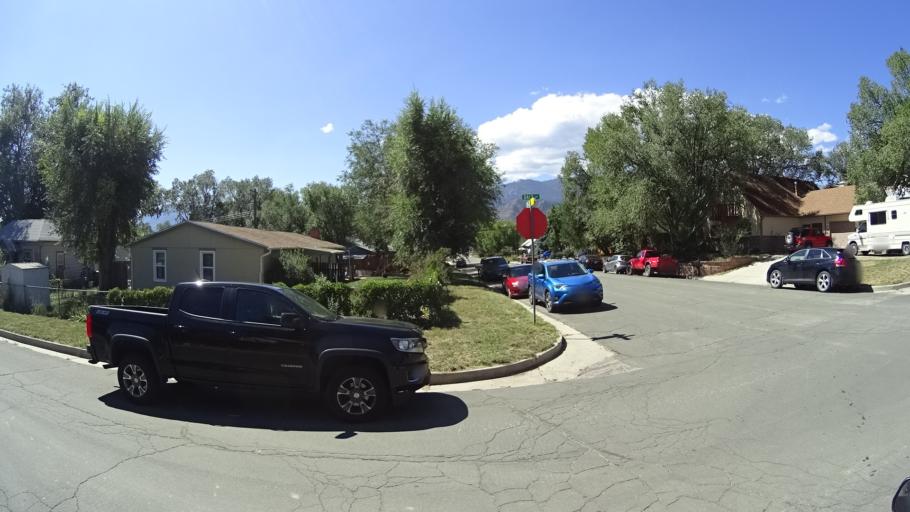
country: US
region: Colorado
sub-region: El Paso County
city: Colorado Springs
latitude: 38.8534
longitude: -104.8564
